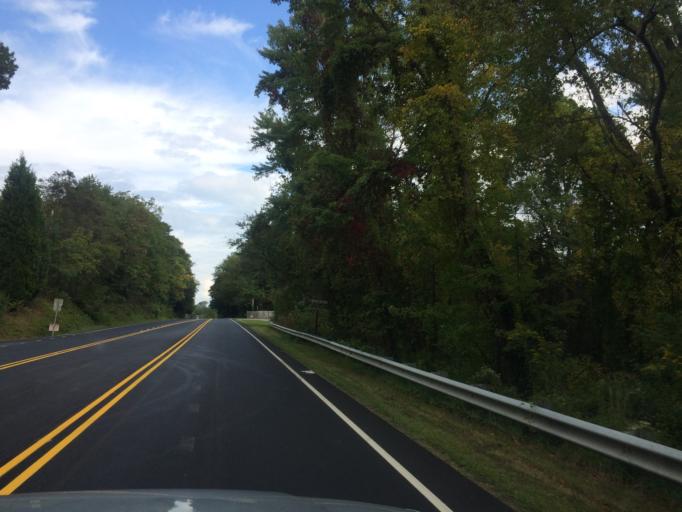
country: US
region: North Carolina
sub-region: Haywood County
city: Canton
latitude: 35.5396
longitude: -82.7604
